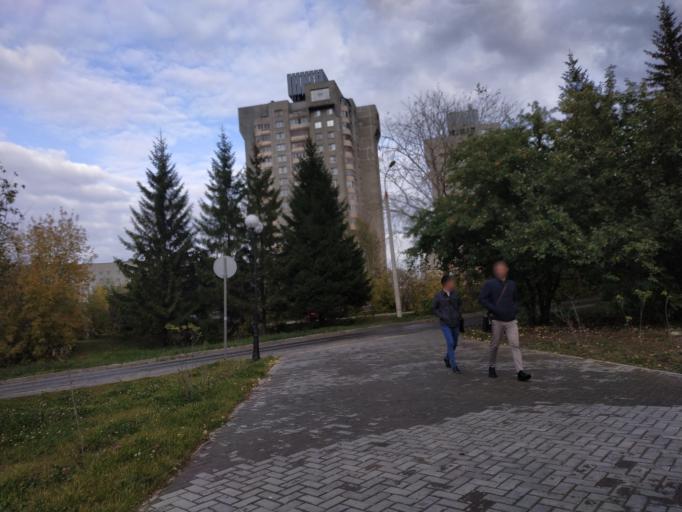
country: RU
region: Chuvashia
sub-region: Cheboksarskiy Rayon
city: Cheboksary
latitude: 56.1465
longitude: 47.2149
